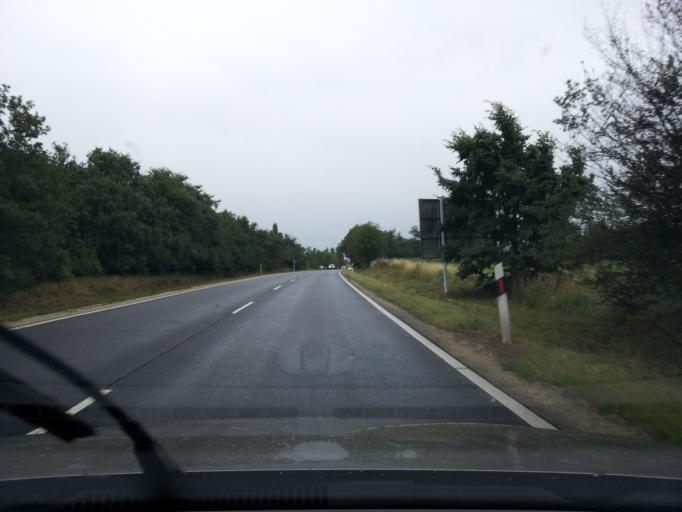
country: HU
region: Fejer
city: Lepseny
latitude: 47.0026
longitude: 18.1776
